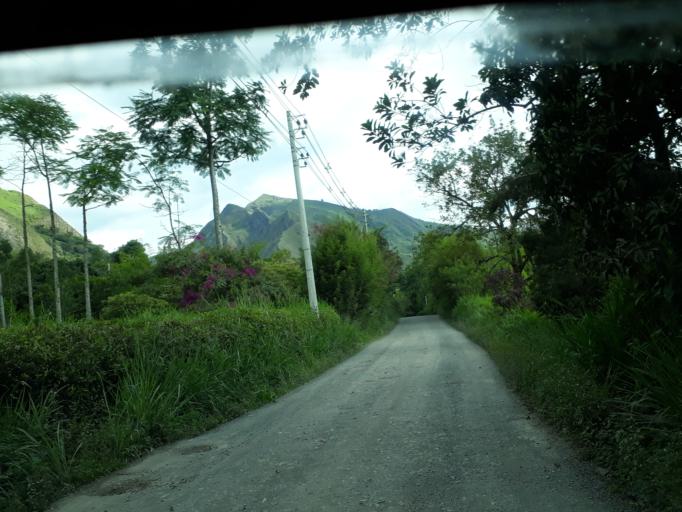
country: CO
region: Cundinamarca
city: Pacho
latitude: 5.1896
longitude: -74.1940
